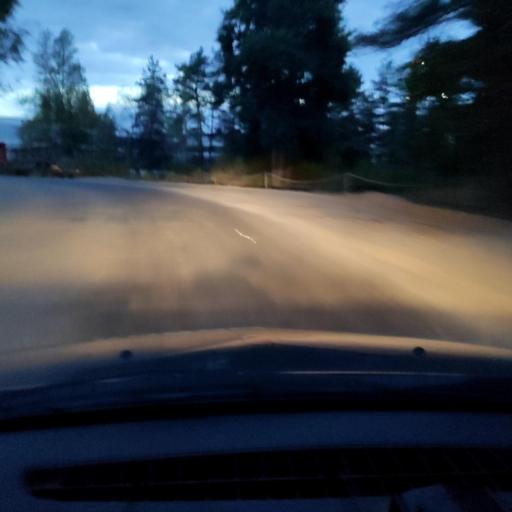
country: RU
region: Voronezj
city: Pridonskoy
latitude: 51.6776
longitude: 39.0919
